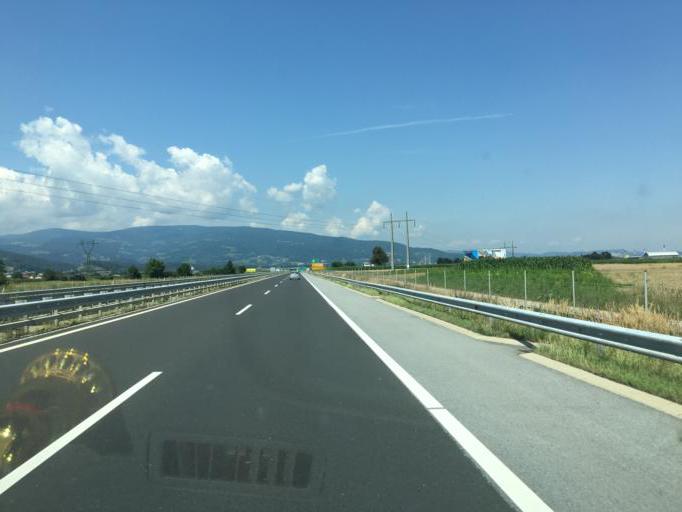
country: SI
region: Race-Fram
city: Race
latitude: 46.4675
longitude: 15.6889
